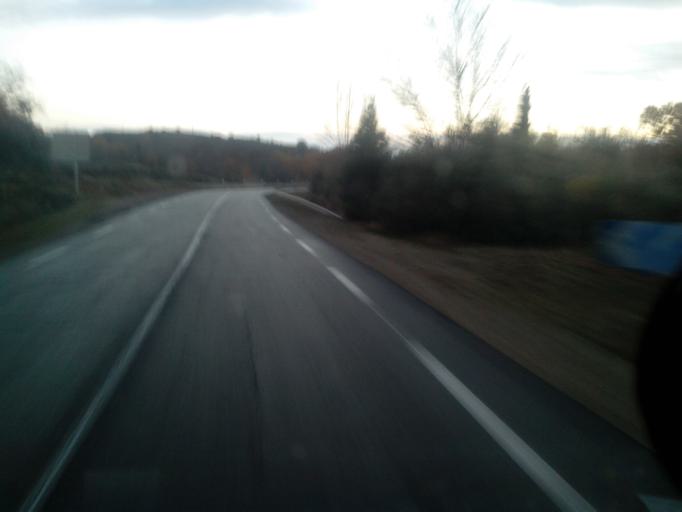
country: FR
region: Languedoc-Roussillon
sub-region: Departement de l'Herault
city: Gignac
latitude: 43.6651
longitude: 3.5662
